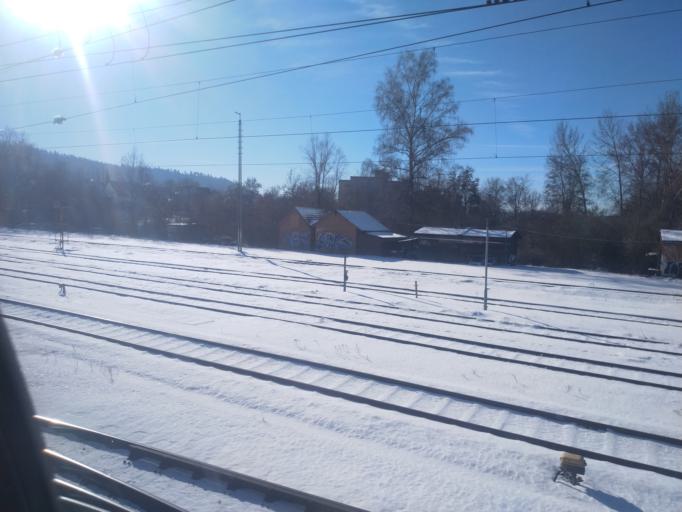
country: DE
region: Baden-Wuerttemberg
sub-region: Freiburg Region
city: Rottweil
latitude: 48.1643
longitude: 8.6473
